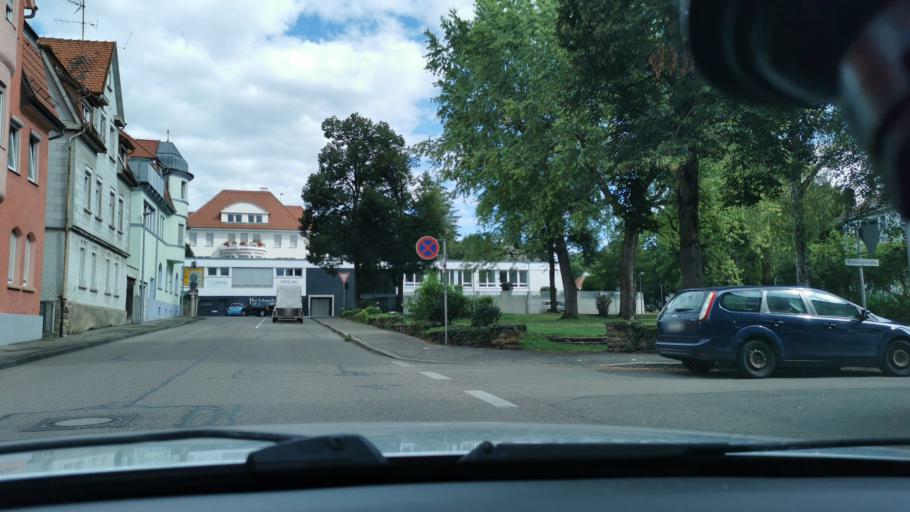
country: DE
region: Baden-Wuerttemberg
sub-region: Regierungsbezirk Stuttgart
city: Goeppingen
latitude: 48.7081
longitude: 9.6605
